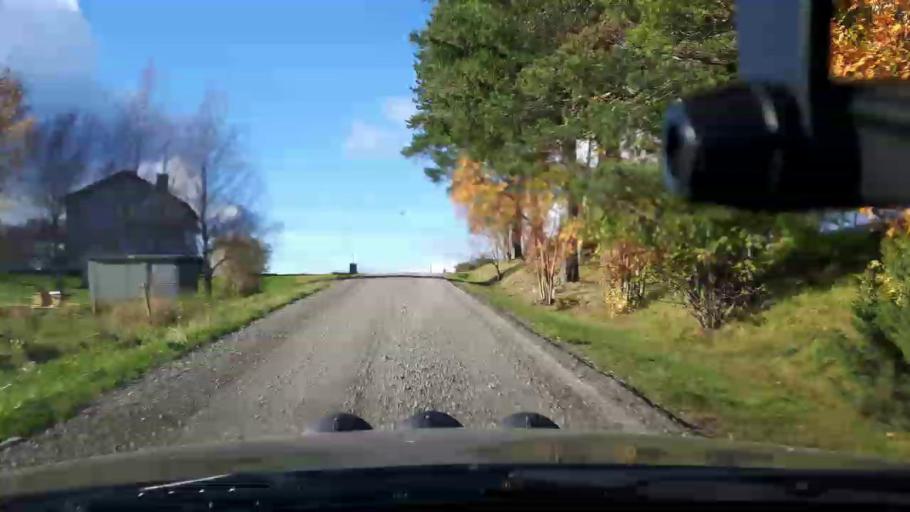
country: SE
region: Jaemtland
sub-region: Bergs Kommun
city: Hoverberg
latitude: 63.0203
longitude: 14.3045
